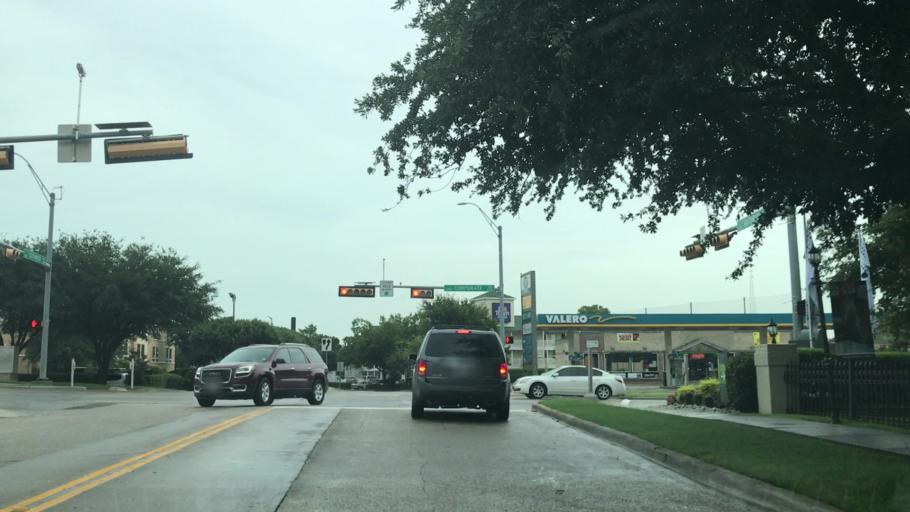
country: US
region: Texas
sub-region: Denton County
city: Lewisville
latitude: 33.0171
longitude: -96.9852
